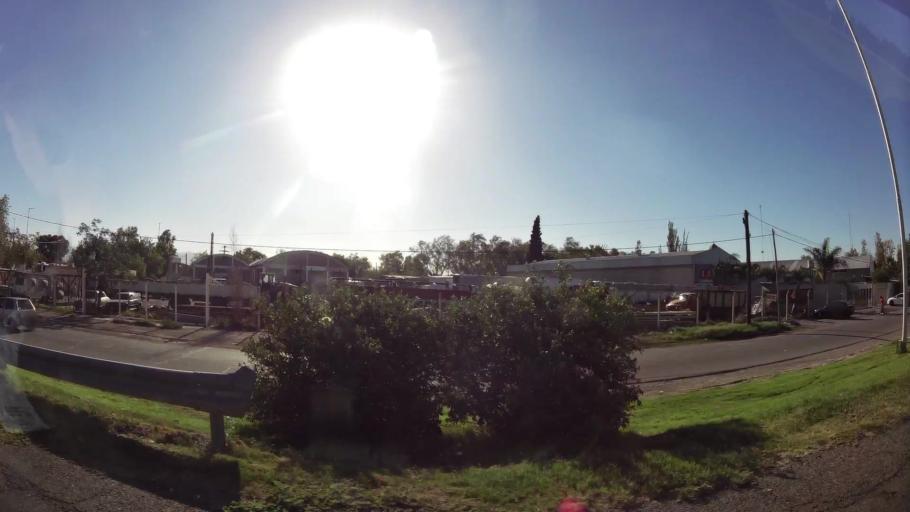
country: AR
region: San Juan
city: Villa Krause
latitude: -31.5716
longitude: -68.5179
